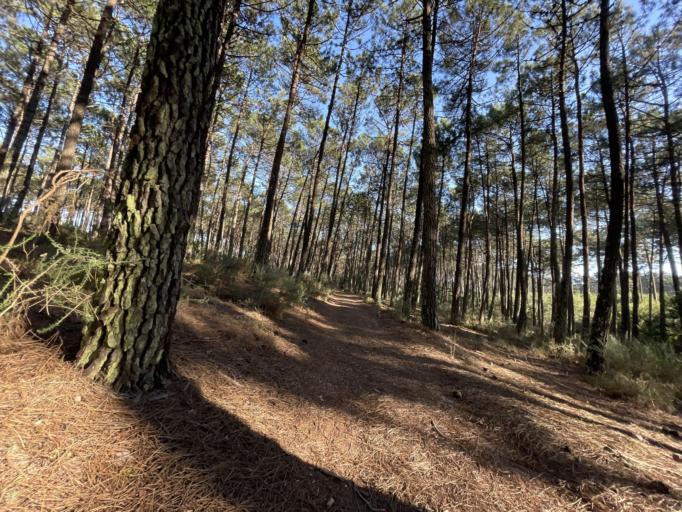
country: PT
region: Aveiro
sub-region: Ovar
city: Cortegaca
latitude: 40.9369
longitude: -8.6416
